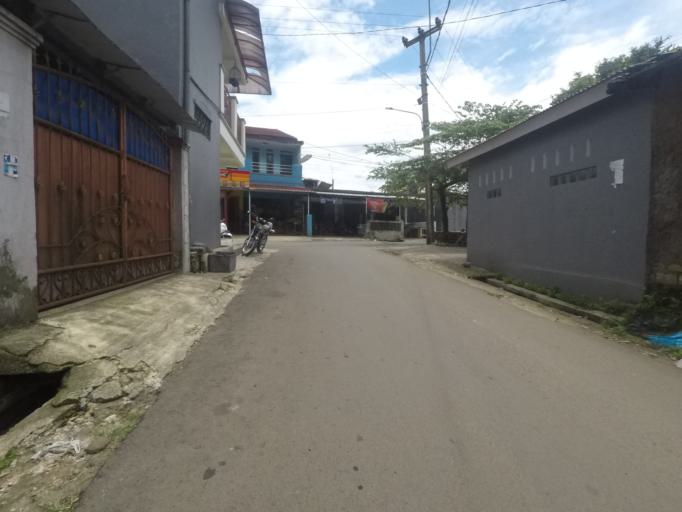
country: ID
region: West Java
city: Bogor
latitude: -6.5570
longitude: 106.7535
